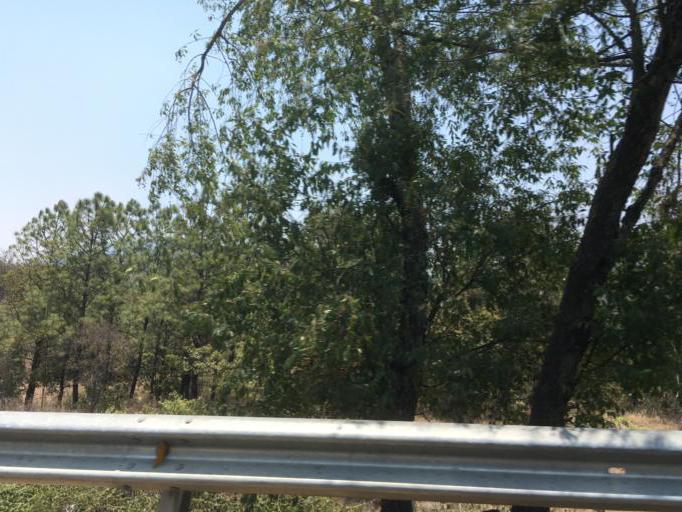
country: MX
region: Michoacan
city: Quiroga
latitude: 19.6568
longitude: -101.5002
